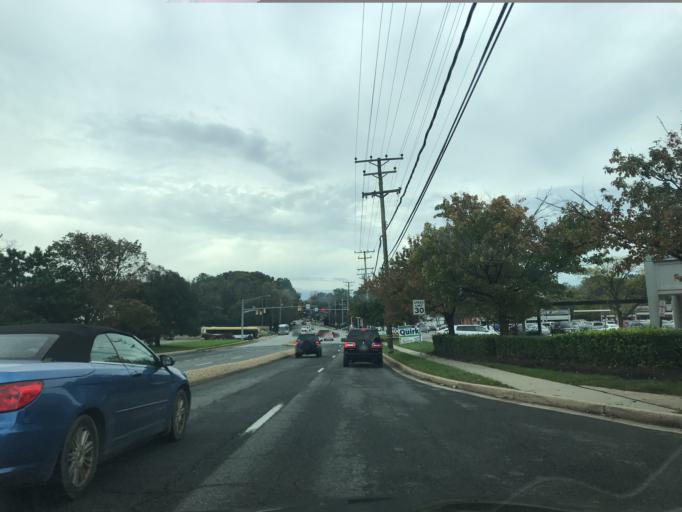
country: US
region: Maryland
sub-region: Baltimore County
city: Catonsville
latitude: 39.2831
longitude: -76.7536
